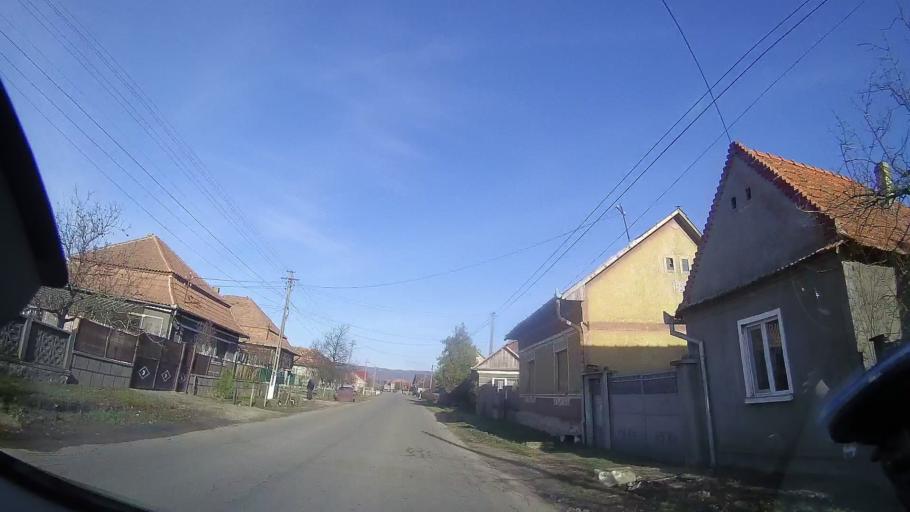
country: RO
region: Bihor
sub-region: Comuna Astileu
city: Astileu
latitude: 47.0308
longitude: 22.3881
